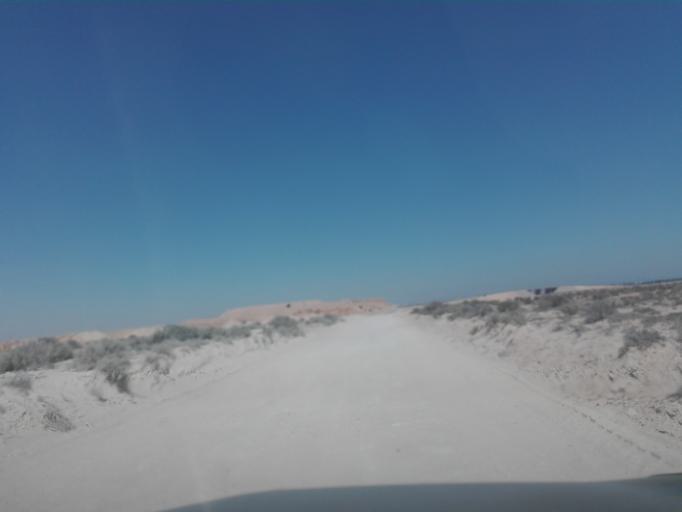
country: TN
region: Qabis
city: Gabes
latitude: 33.8638
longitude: 10.0049
